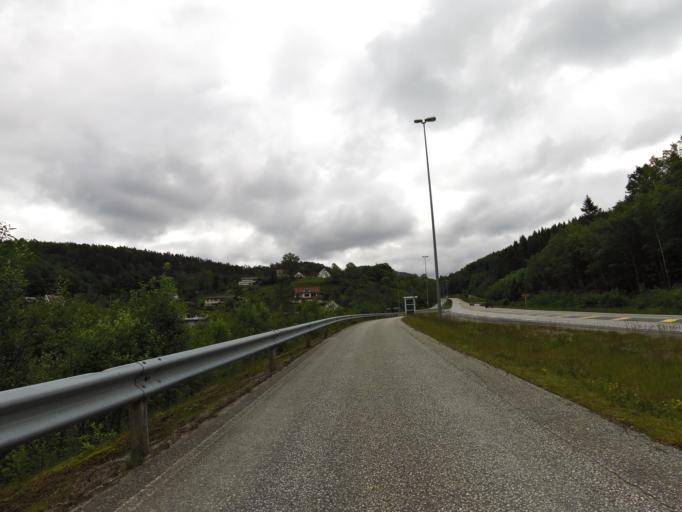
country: NO
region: Vest-Agder
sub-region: Flekkefjord
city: Flekkefjord
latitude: 58.2952
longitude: 6.6888
